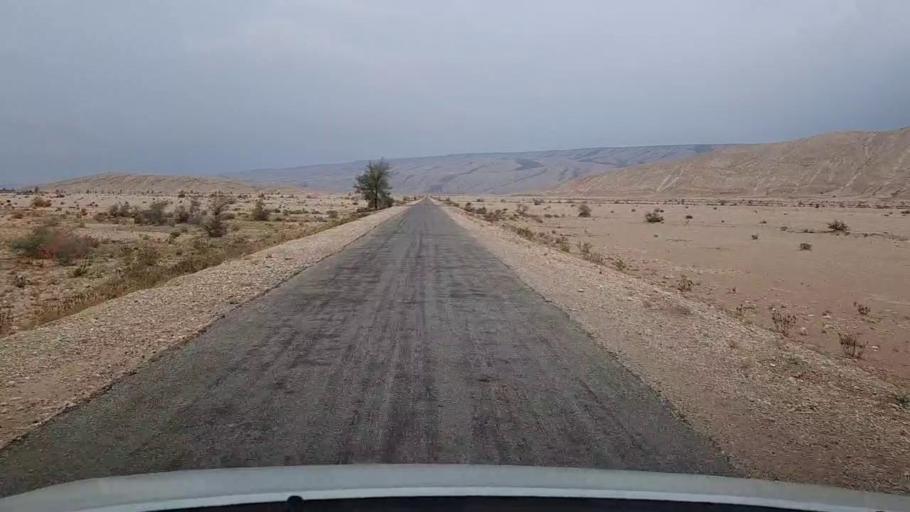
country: PK
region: Sindh
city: Sehwan
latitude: 26.2403
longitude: 67.7130
